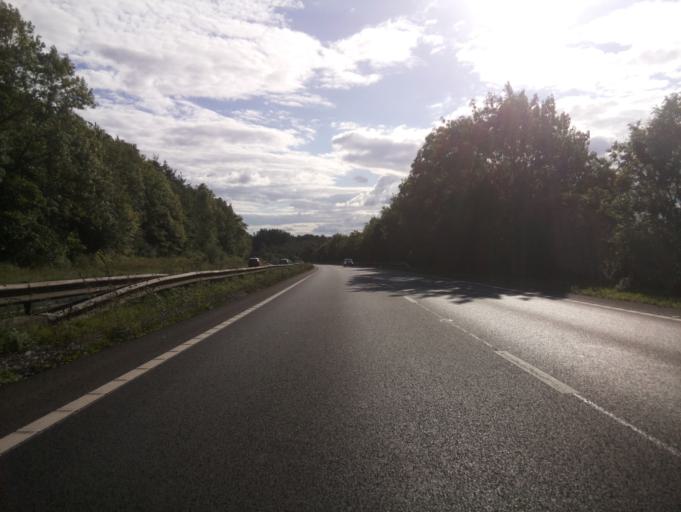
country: GB
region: England
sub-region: Devon
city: Chudleigh
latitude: 50.6151
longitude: -3.5950
